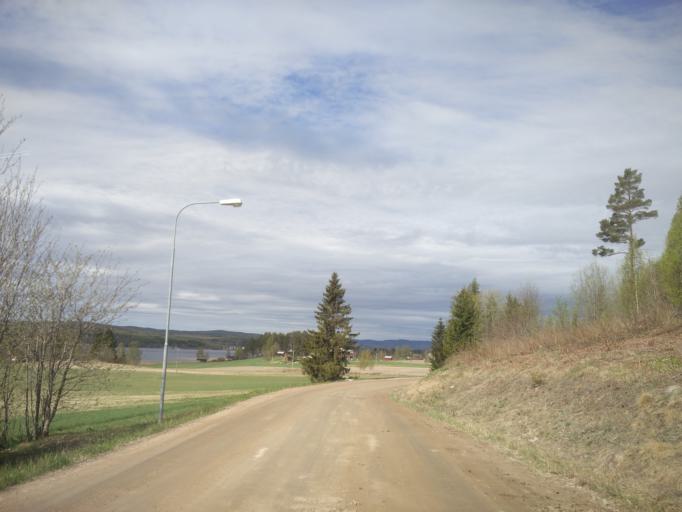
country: SE
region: Vaesternorrland
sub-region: Sundsvalls Kommun
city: Vi
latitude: 62.2737
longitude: 17.1476
